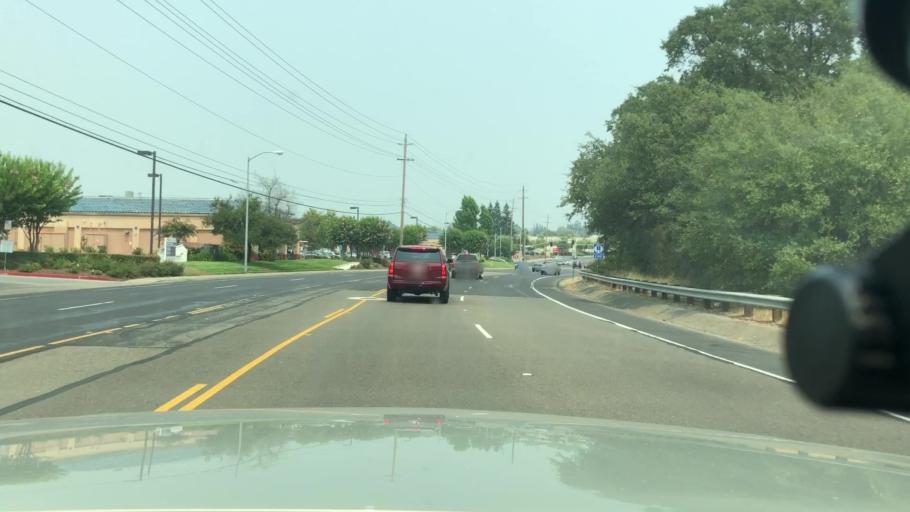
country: US
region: California
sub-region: Sacramento County
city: Folsom
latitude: 38.6674
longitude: -121.1551
